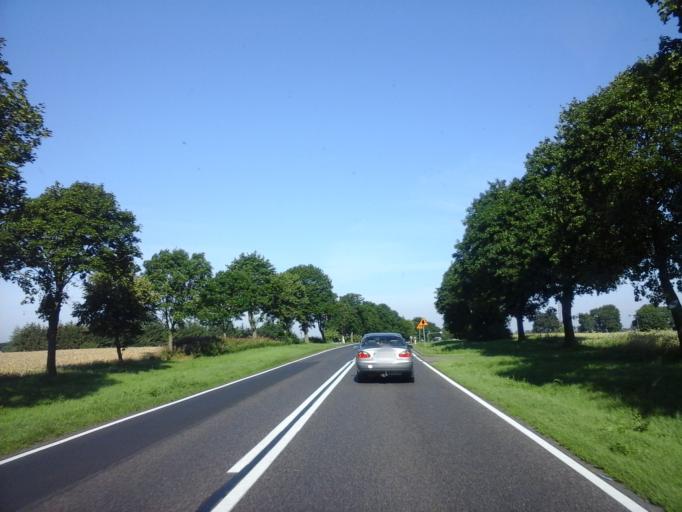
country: PL
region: West Pomeranian Voivodeship
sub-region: Powiat stargardzki
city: Stargard Szczecinski
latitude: 53.3092
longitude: 15.1257
